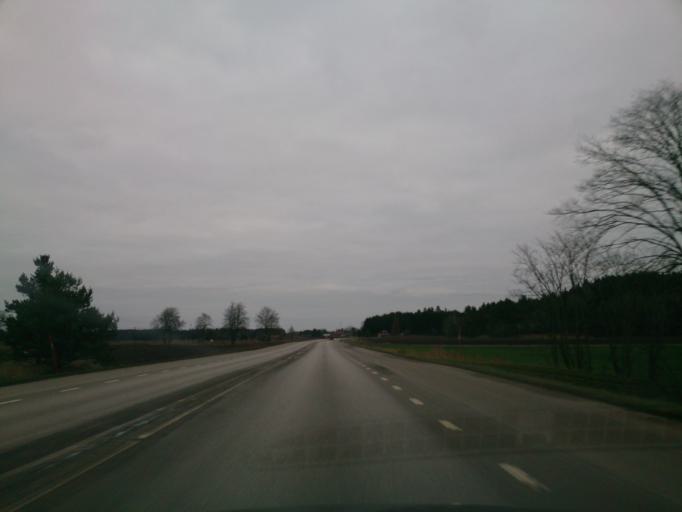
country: SE
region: OEstergoetland
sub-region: Norrkopings Kommun
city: Kimstad
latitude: 58.4699
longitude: 15.8972
